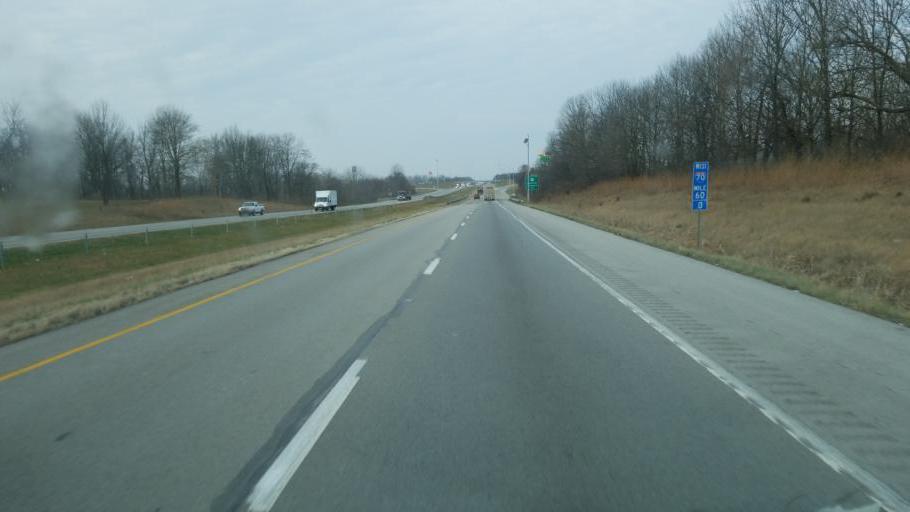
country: US
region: Indiana
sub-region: Morgan County
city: Monrovia
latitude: 39.6168
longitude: -86.4698
